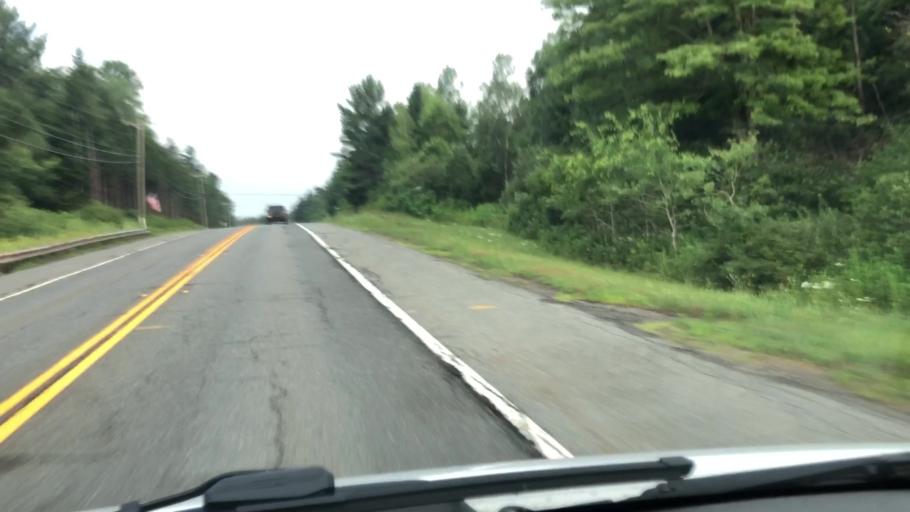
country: US
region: Massachusetts
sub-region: Berkshire County
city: Hinsdale
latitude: 42.5113
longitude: -73.0769
